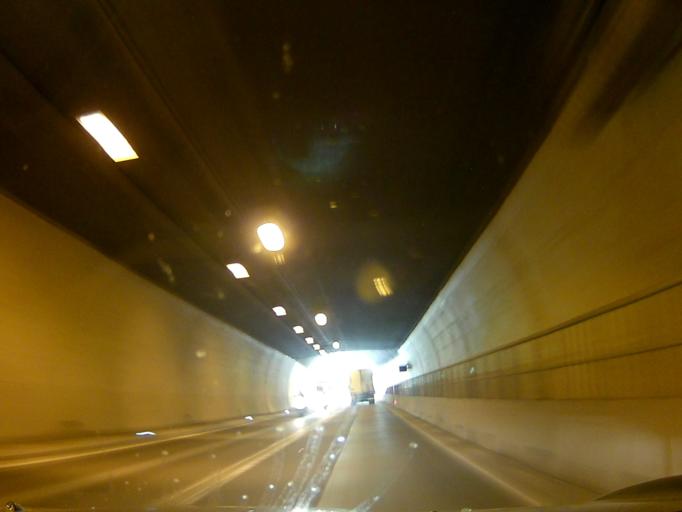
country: AT
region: Salzburg
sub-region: Politischer Bezirk Zell am See
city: Lend
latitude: 47.2893
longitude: 13.0614
